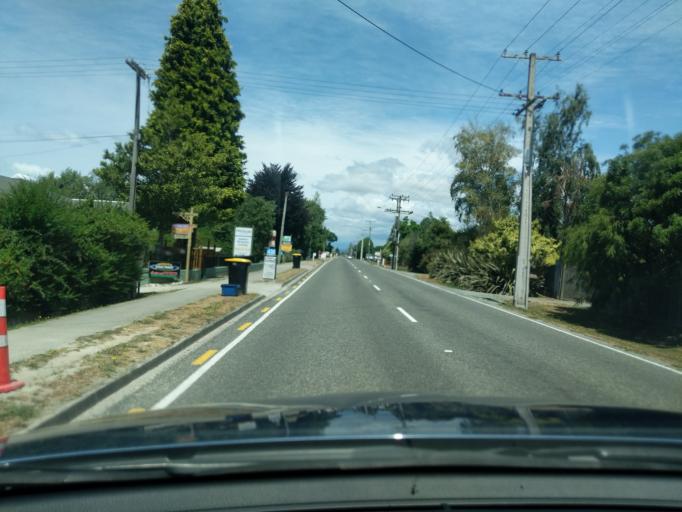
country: NZ
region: Tasman
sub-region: Tasman District
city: Motueka
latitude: -41.0836
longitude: 172.9970
